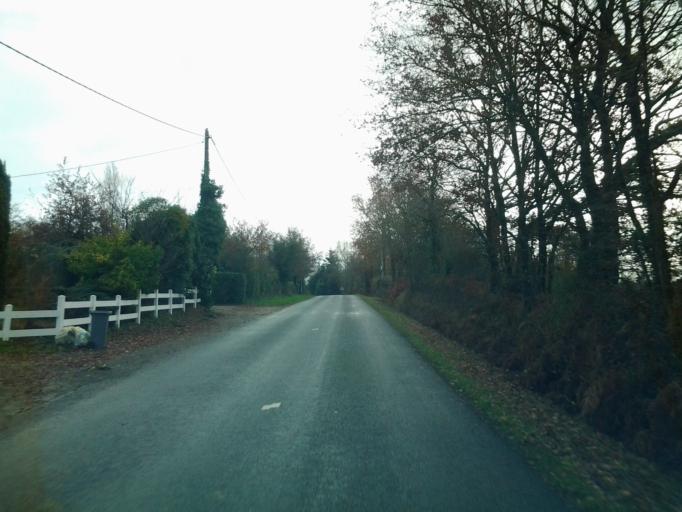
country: FR
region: Pays de la Loire
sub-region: Departement de la Vendee
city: Nesmy
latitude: 46.6456
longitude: -1.3720
